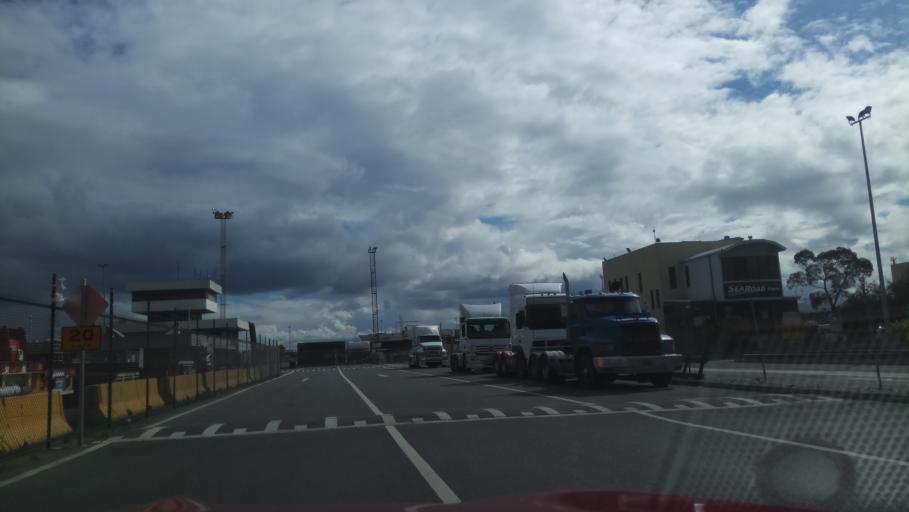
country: AU
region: Victoria
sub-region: Hobsons Bay
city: Williamstown
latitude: -37.8417
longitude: 144.9108
